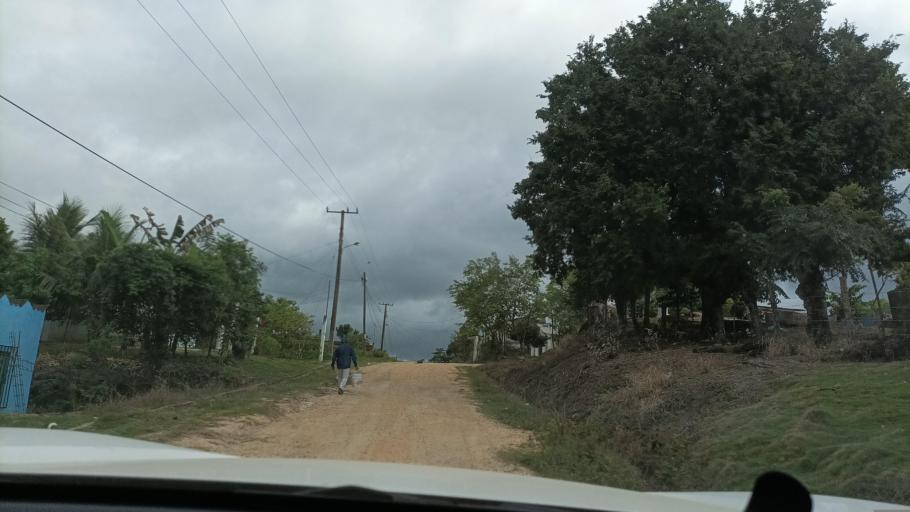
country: MX
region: Veracruz
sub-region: Jaltipan
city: Las Lomas de Tacamichapan
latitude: 17.8649
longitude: -94.7101
